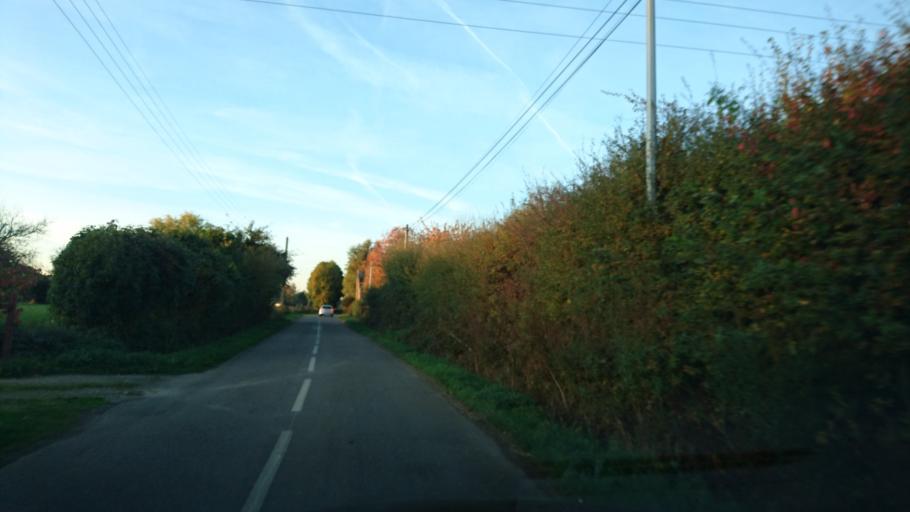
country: FR
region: Brittany
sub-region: Departement d'Ille-et-Vilaine
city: Bruz
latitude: 48.0048
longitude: -1.7546
